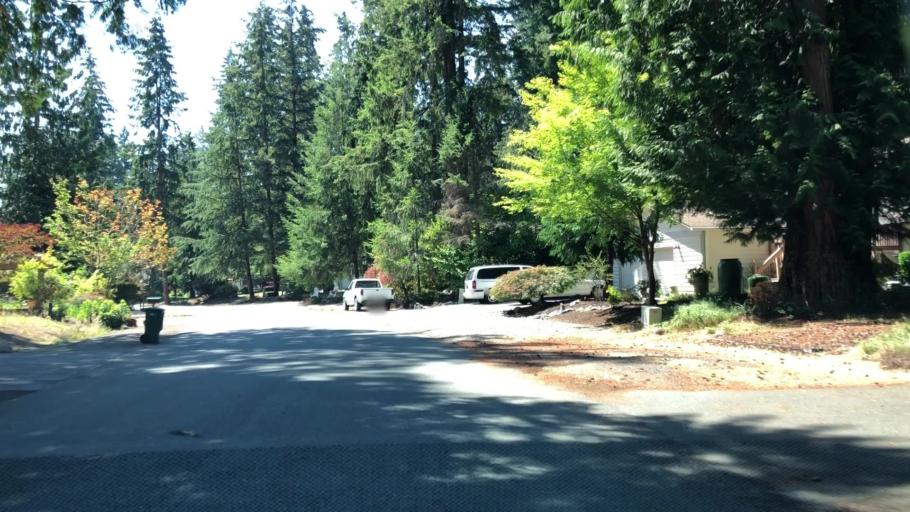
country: US
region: Washington
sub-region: King County
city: Cottage Lake
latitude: 47.7493
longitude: -122.0861
